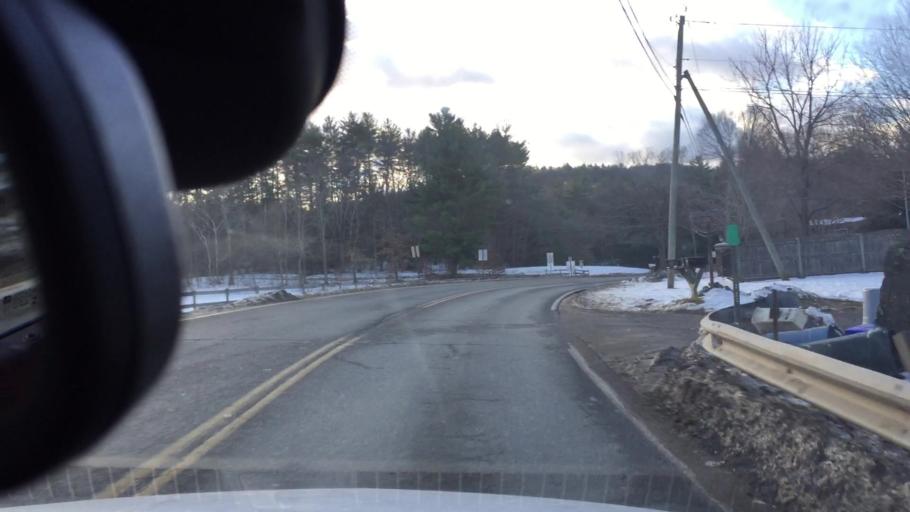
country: US
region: Massachusetts
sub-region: Franklin County
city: Montague
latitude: 42.5102
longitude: -72.5369
